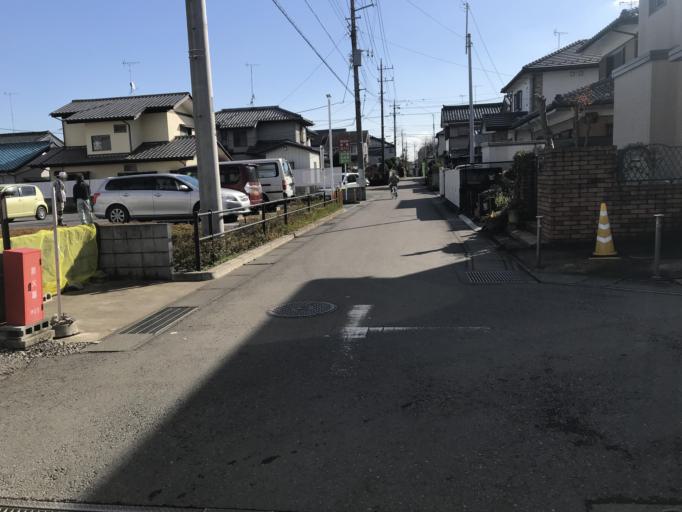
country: JP
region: Ibaraki
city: Ushiku
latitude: 35.9746
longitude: 140.1491
